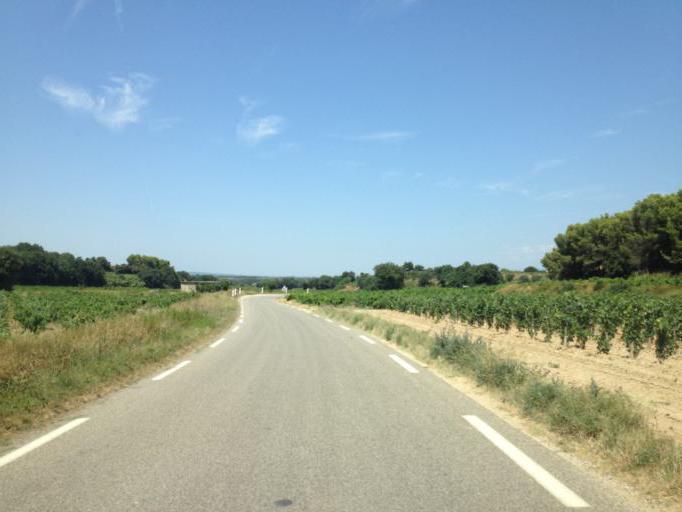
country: FR
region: Provence-Alpes-Cote d'Azur
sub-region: Departement du Vaucluse
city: Courthezon
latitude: 44.0715
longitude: 4.8619
